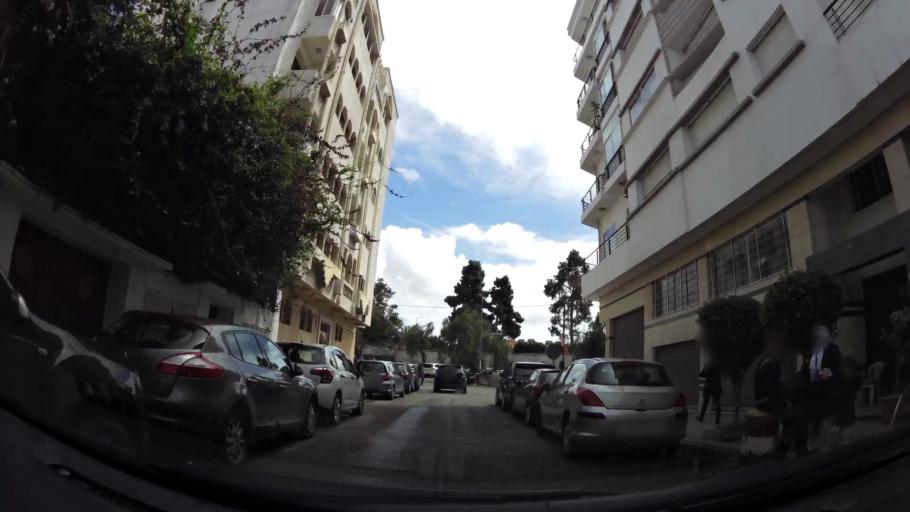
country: MA
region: Grand Casablanca
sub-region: Casablanca
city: Casablanca
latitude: 33.5789
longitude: -7.6221
